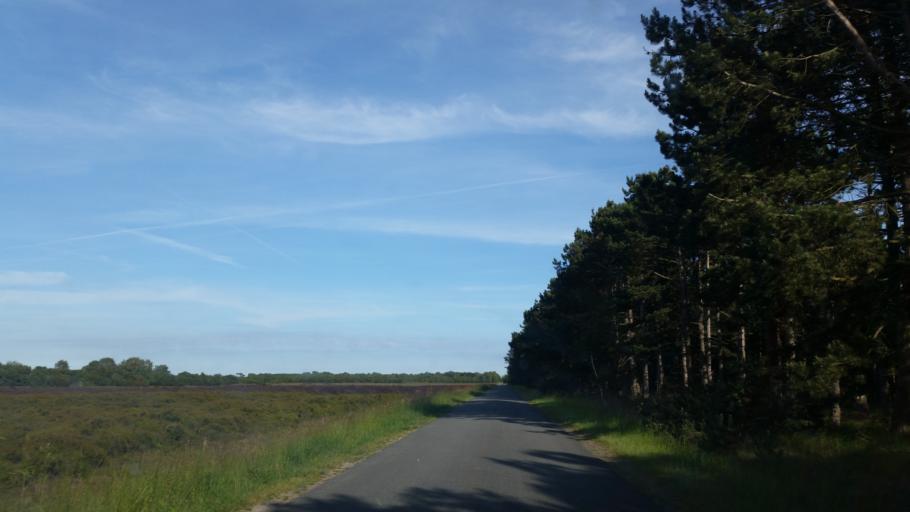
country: DK
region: Central Jutland
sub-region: Samso Kommune
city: Tranebjerg
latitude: 55.9243
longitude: 10.5995
